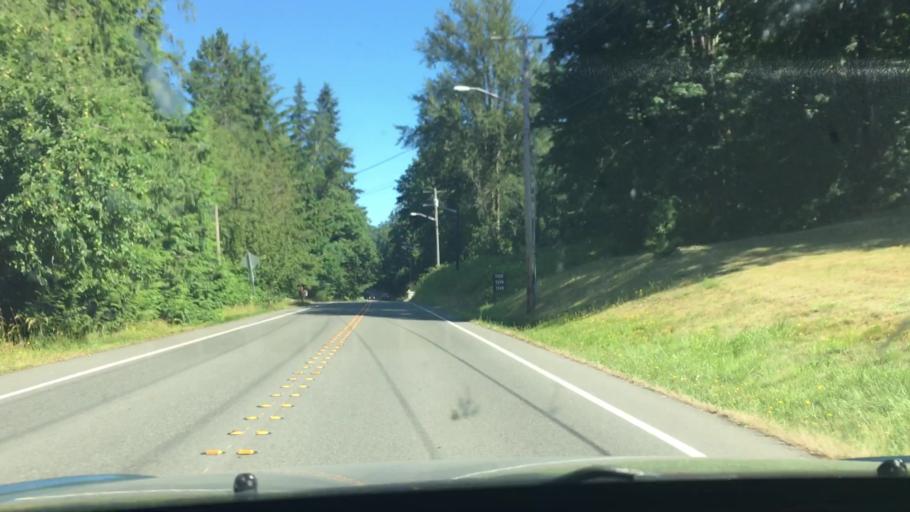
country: US
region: Washington
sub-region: King County
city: Newcastle
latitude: 47.5368
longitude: -122.1287
